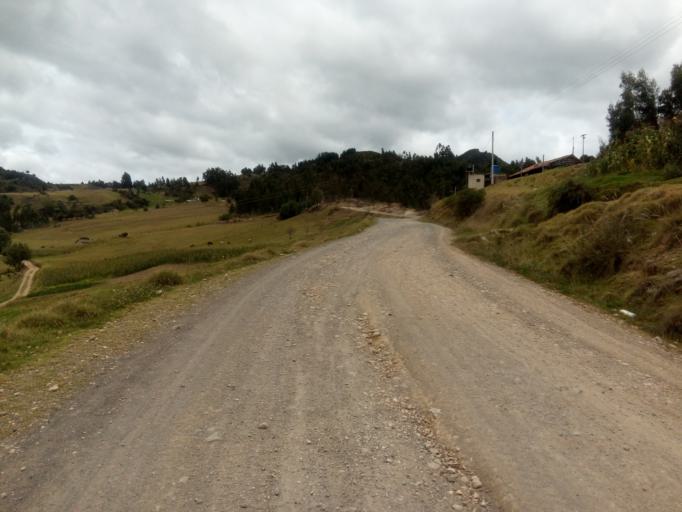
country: CO
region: Boyaca
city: Gameza
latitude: 5.8104
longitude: -72.8049
